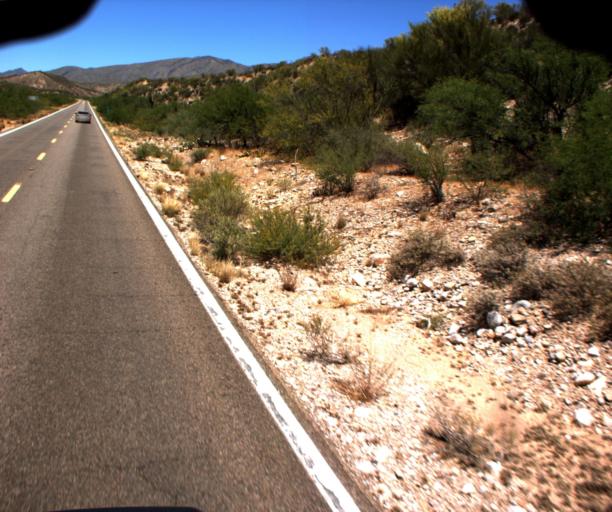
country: US
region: Arizona
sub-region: Pinal County
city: Kearny
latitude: 33.1182
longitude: -110.7718
